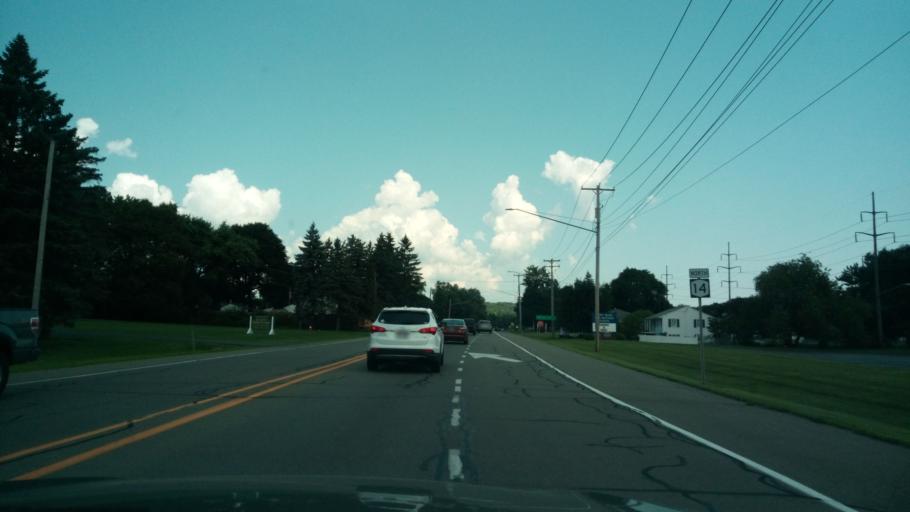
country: US
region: New York
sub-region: Chemung County
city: Horseheads
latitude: 42.1658
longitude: -76.8401
